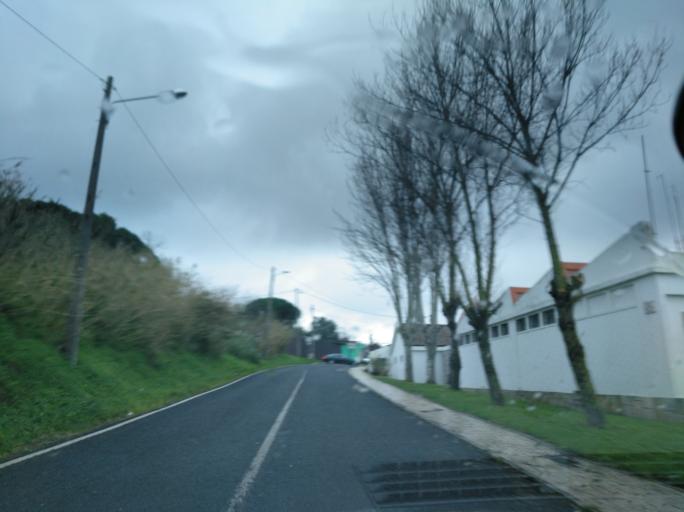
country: PT
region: Lisbon
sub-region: Odivelas
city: Pontinha
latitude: 38.7707
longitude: -9.1951
